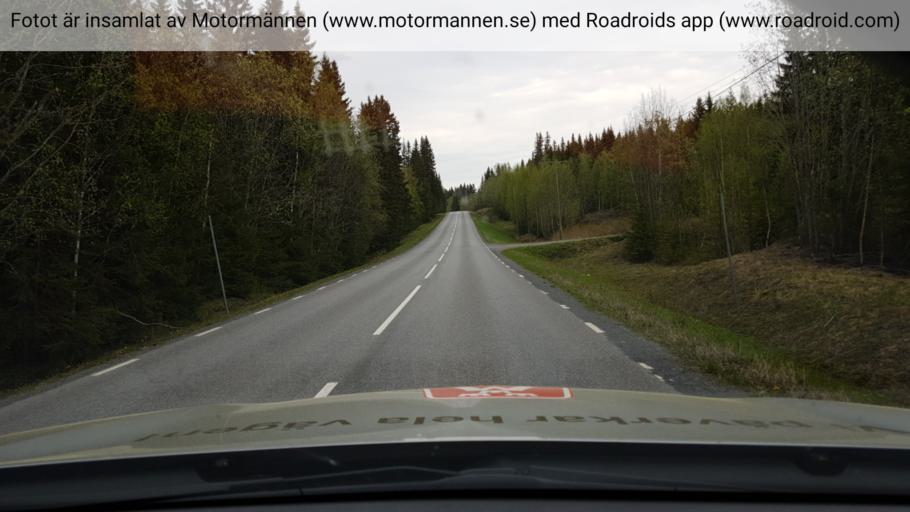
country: SE
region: Jaemtland
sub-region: Are Kommun
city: Jarpen
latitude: 63.4428
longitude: 13.3840
